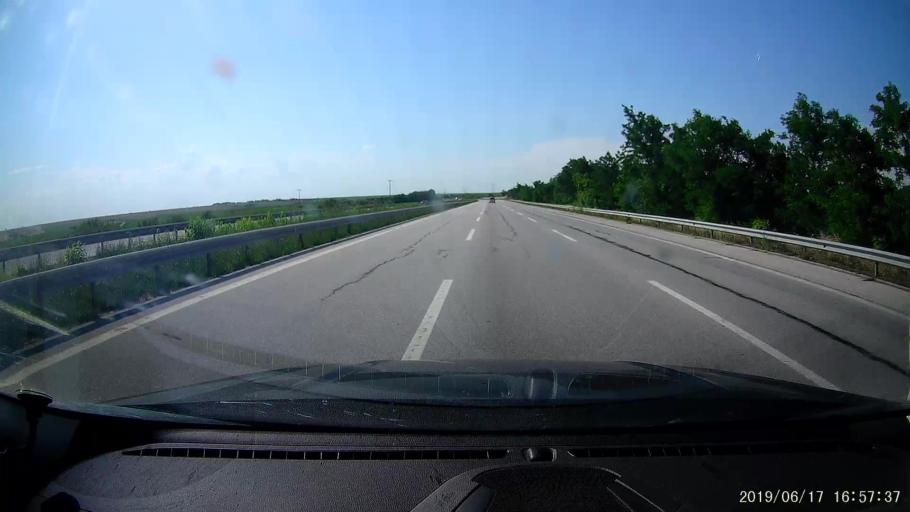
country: TR
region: Edirne
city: Haskoy
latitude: 41.6036
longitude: 26.9104
